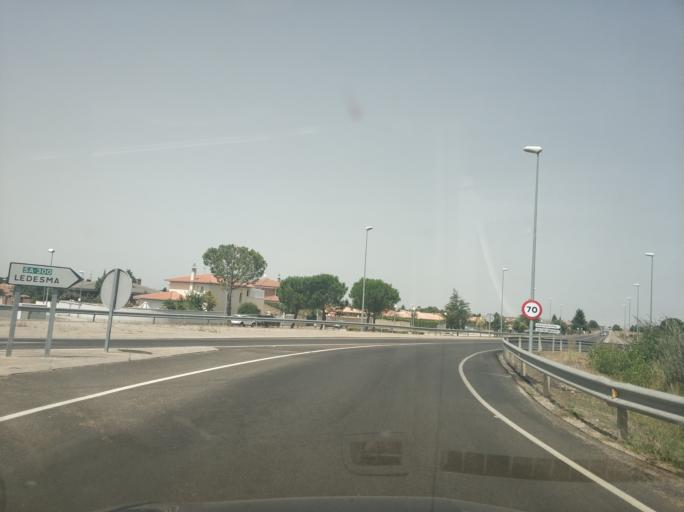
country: ES
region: Castille and Leon
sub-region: Provincia de Salamanca
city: Villamayor
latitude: 41.0094
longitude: -5.7073
